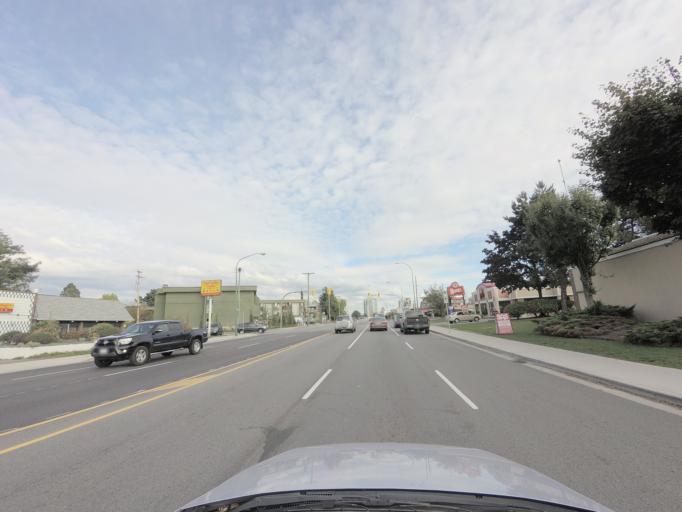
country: CA
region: British Columbia
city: Burnaby
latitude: 49.2208
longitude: -122.9759
